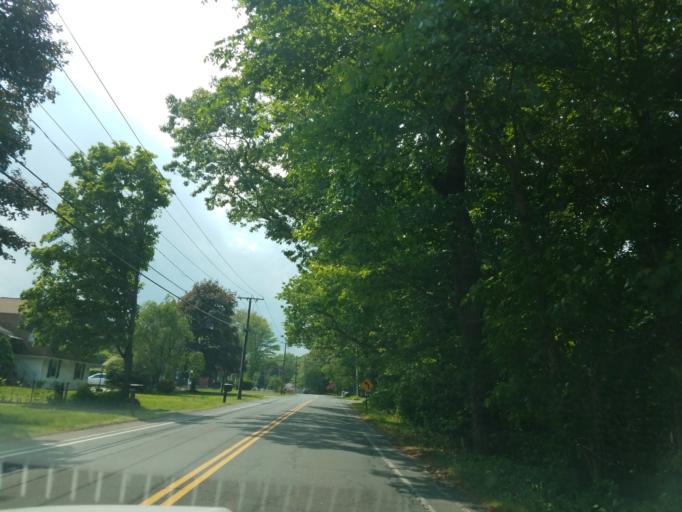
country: US
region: Massachusetts
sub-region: Hampden County
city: Agawam
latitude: 42.0430
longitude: -72.6256
